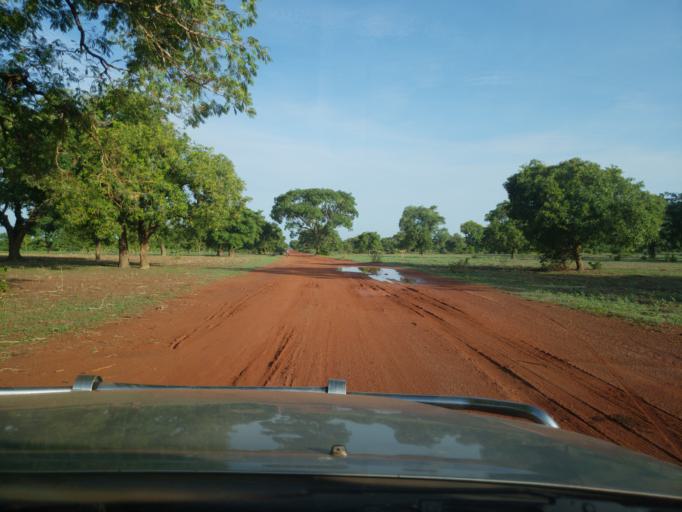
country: ML
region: Sikasso
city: Koutiala
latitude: 12.4255
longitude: -5.5955
